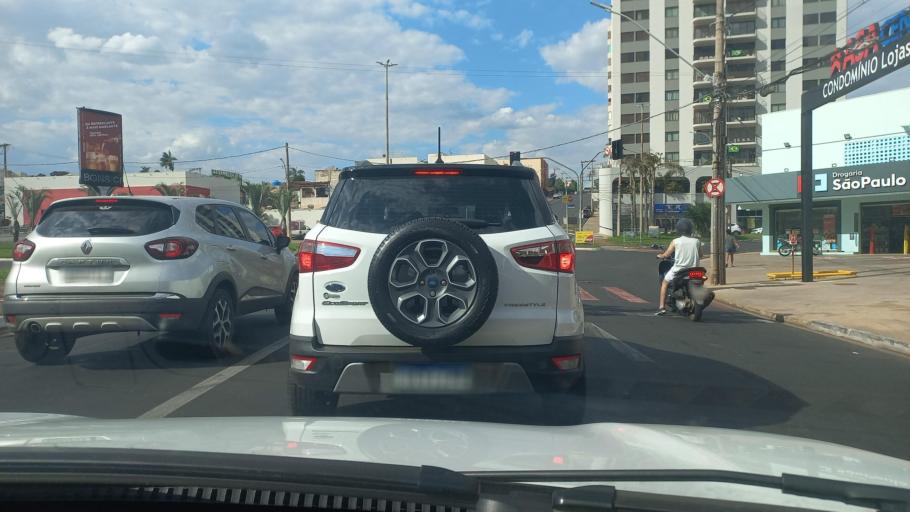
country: BR
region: Minas Gerais
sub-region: Uberaba
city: Uberaba
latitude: -19.7434
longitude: -47.9319
